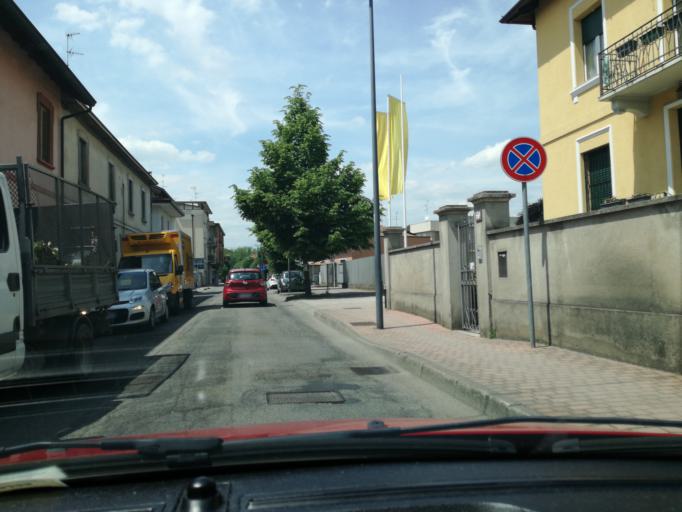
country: IT
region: Lombardy
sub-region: Provincia di Monza e Brianza
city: Limbiate
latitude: 45.6147
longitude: 9.1365
